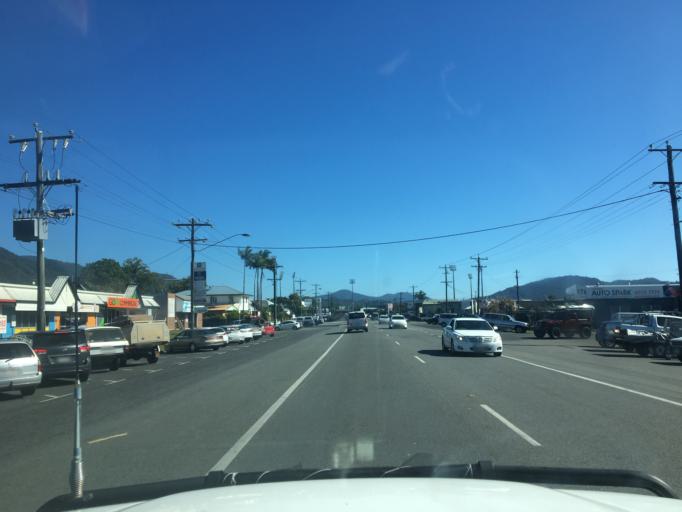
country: AU
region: Queensland
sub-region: Cairns
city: Woree
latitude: -16.9397
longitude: 145.7522
